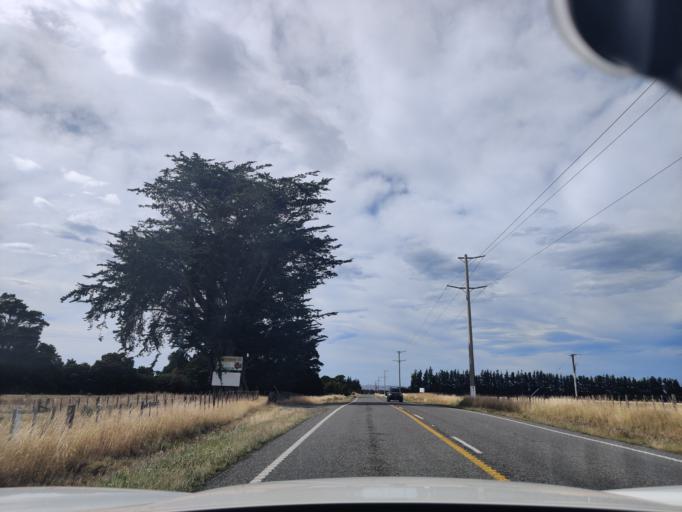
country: NZ
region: Wellington
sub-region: Masterton District
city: Masterton
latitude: -40.8360
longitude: 175.6292
